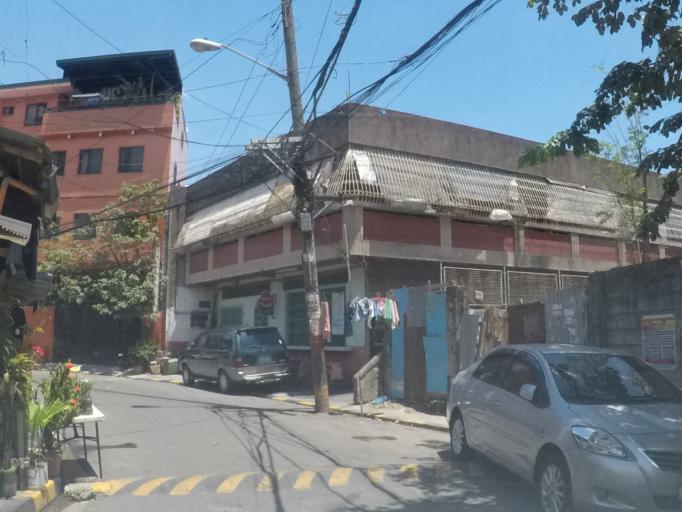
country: PH
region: Metro Manila
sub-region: San Juan
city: San Juan
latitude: 14.6027
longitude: 121.0215
